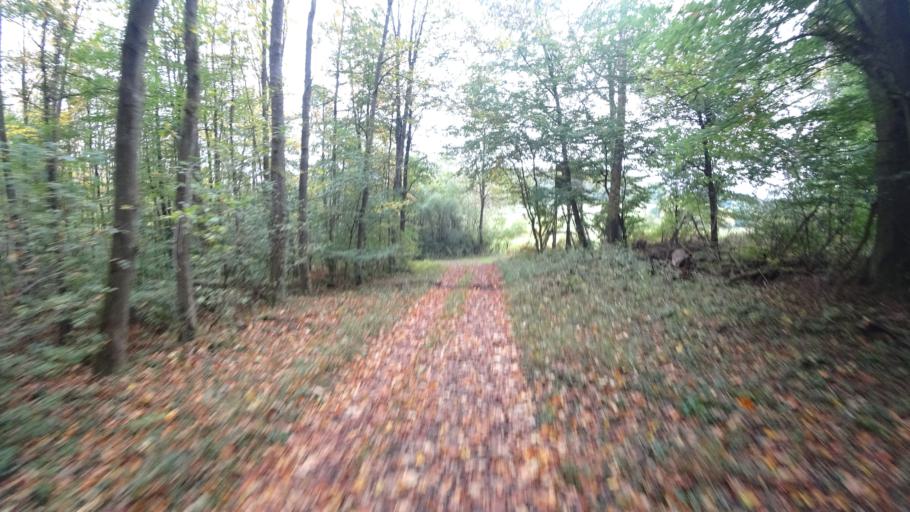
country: DE
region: Rheinland-Pfalz
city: Nordhofen
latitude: 50.5183
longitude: 7.7434
